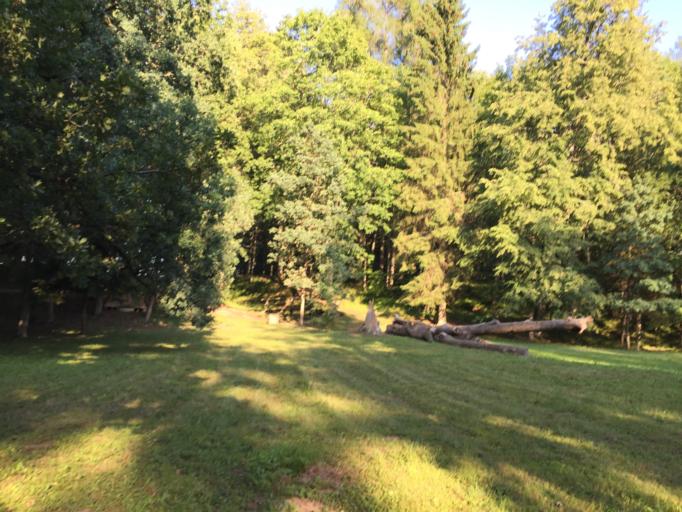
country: LV
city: Tervete
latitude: 56.4190
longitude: 23.5404
